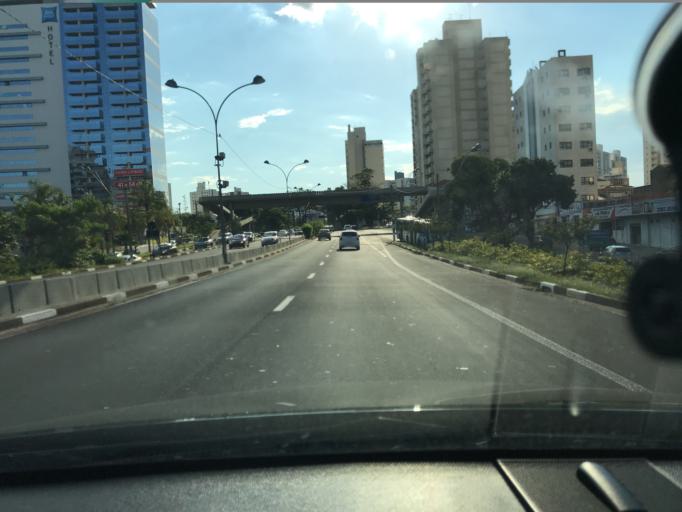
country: BR
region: Sao Paulo
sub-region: Campinas
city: Campinas
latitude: -22.9110
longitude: -47.0568
